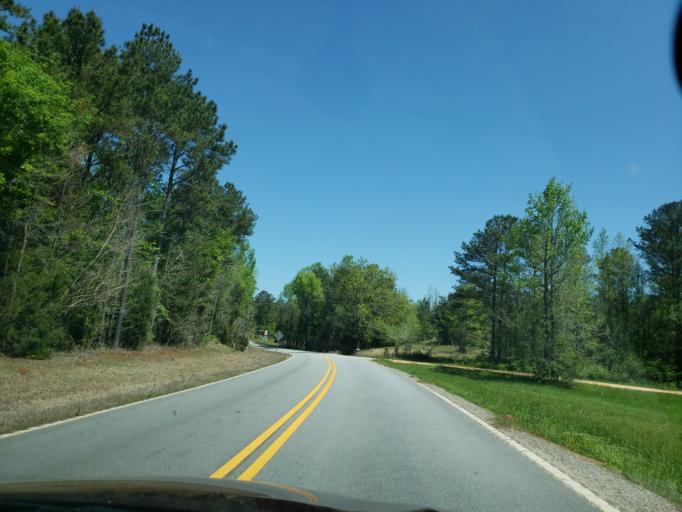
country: US
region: Alabama
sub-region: Tallapoosa County
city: Camp Hill
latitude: 32.7020
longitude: -85.7130
